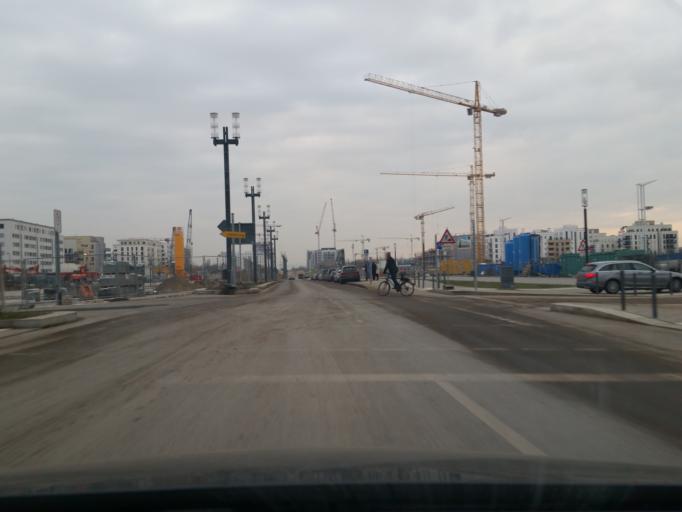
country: DE
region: Hesse
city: Niederrad
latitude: 50.1084
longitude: 8.6404
